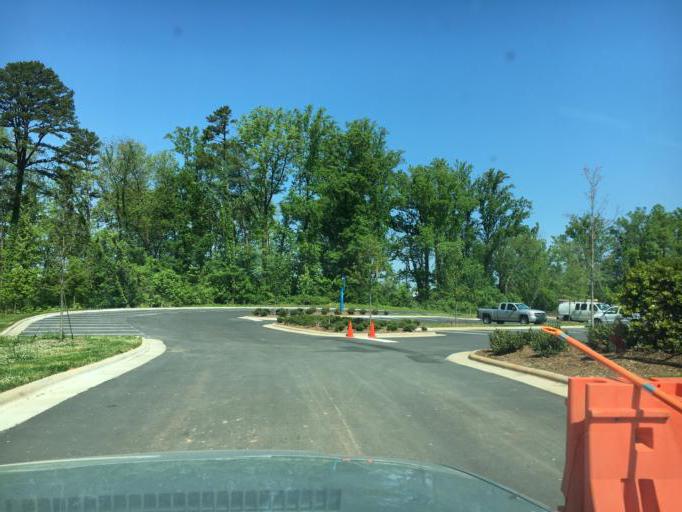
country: US
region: North Carolina
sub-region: Burke County
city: Morganton
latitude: 35.7327
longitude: -81.6800
